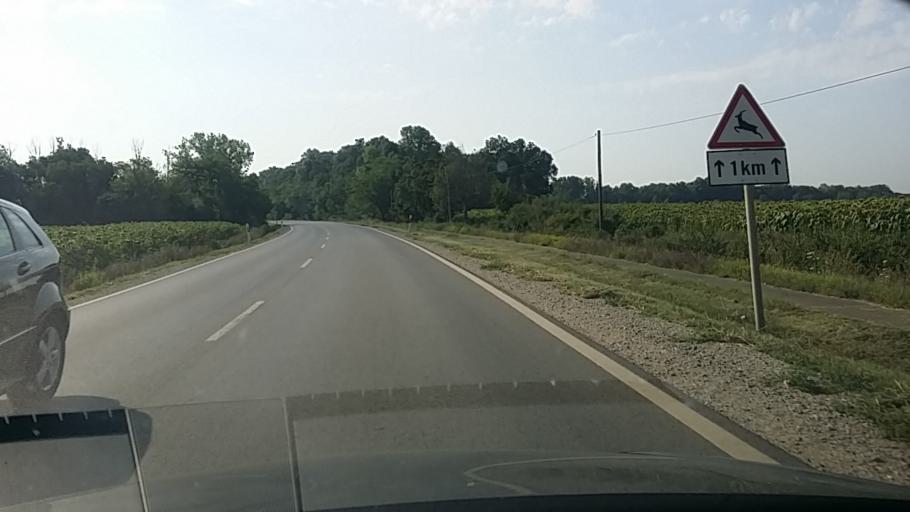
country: HU
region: Bekes
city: Kondoros
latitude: 46.7719
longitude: 20.7564
